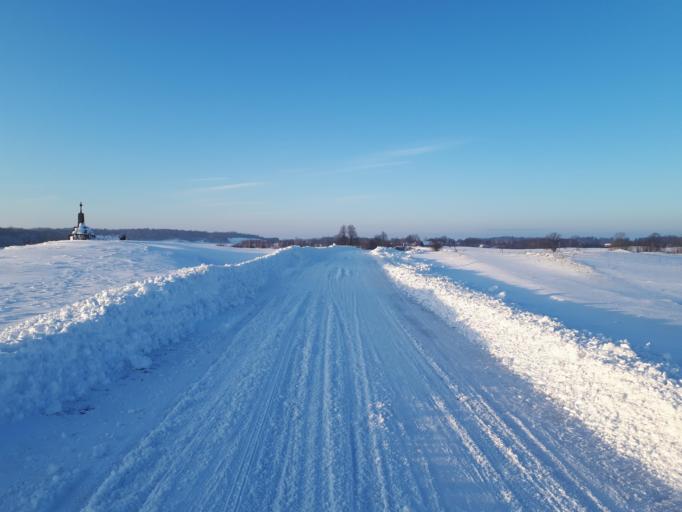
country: LT
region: Alytaus apskritis
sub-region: Alytaus rajonas
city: Daugai
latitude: 54.4850
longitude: 24.2611
